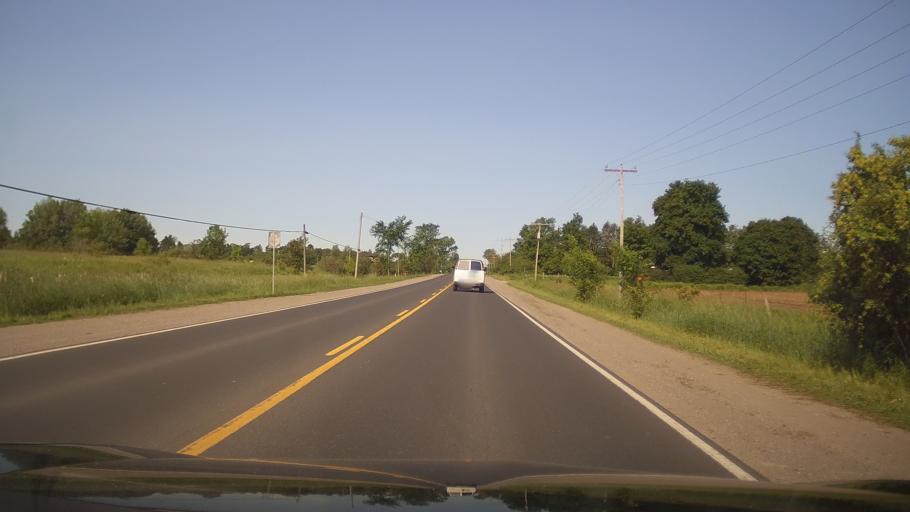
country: CA
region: Ontario
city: Peterborough
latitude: 44.2709
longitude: -78.3917
